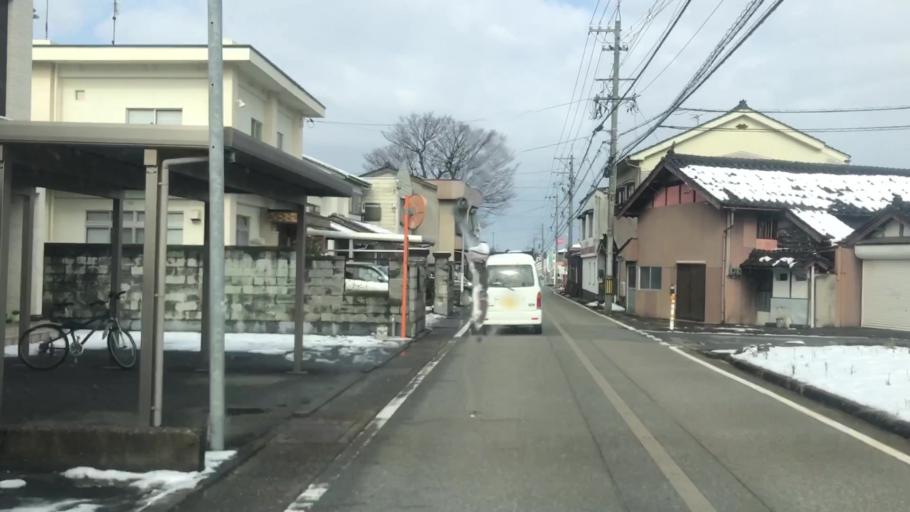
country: JP
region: Toyama
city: Toyama-shi
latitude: 36.6255
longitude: 137.2517
